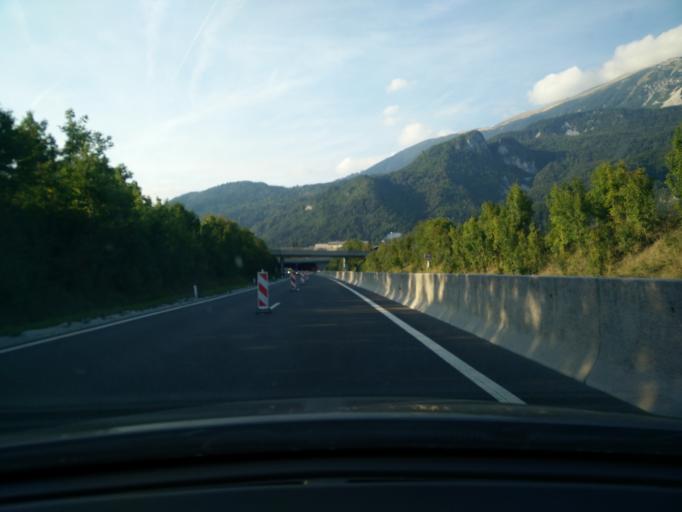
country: SI
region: Zirovnica
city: Zirovnica
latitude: 46.4022
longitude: 14.1306
